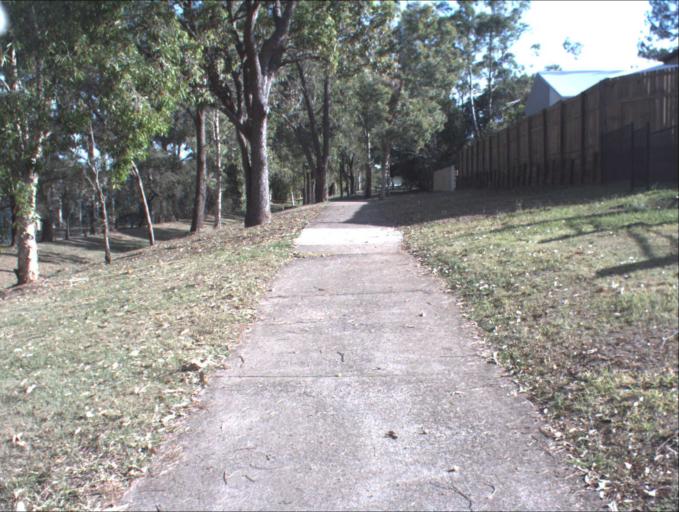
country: AU
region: Queensland
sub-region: Logan
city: Beenleigh
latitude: -27.6764
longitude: 153.2058
